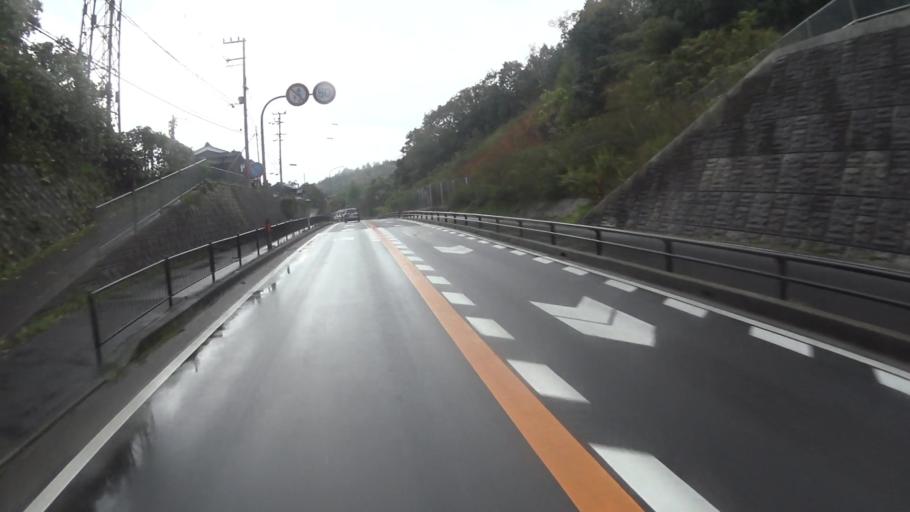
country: JP
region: Kyoto
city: Ayabe
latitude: 35.1884
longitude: 135.3210
